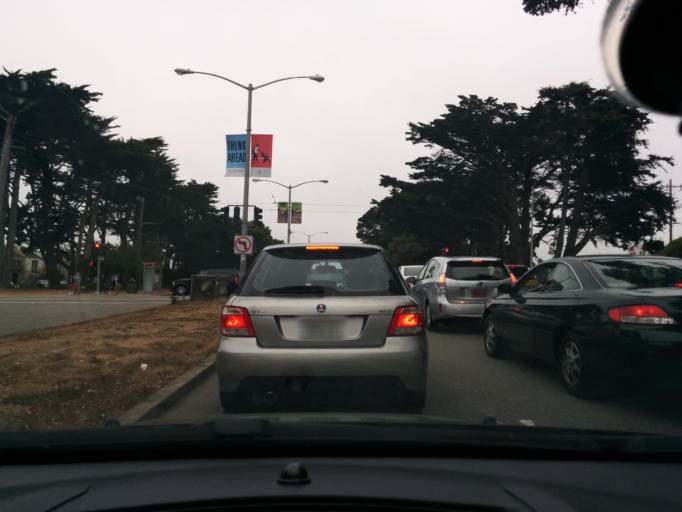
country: US
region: California
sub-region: San Mateo County
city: Daly City
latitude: 37.7420
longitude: -122.4944
